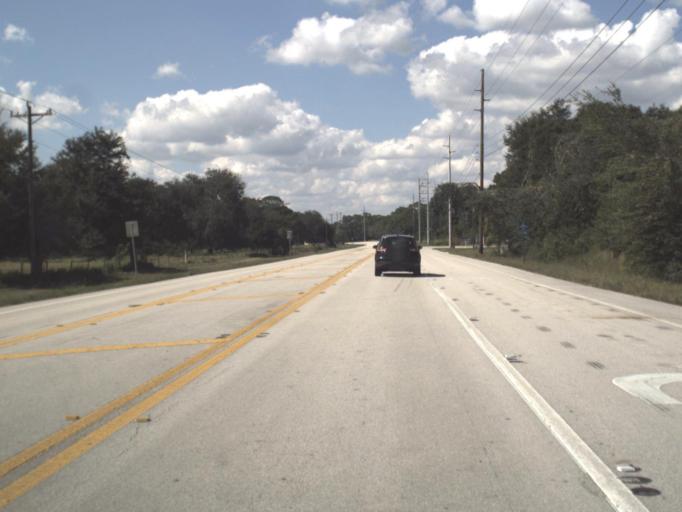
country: US
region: Florida
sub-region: Highlands County
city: Sebring
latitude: 27.4344
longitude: -81.3643
